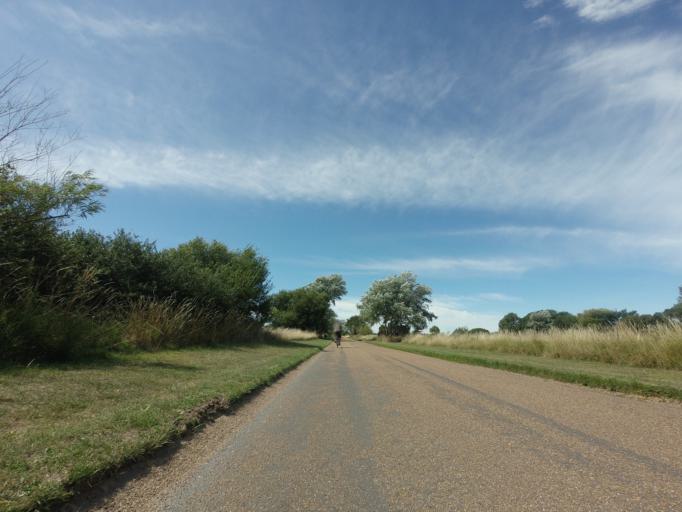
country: GB
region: England
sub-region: Kent
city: Sandwich
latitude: 51.2674
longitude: 1.3775
